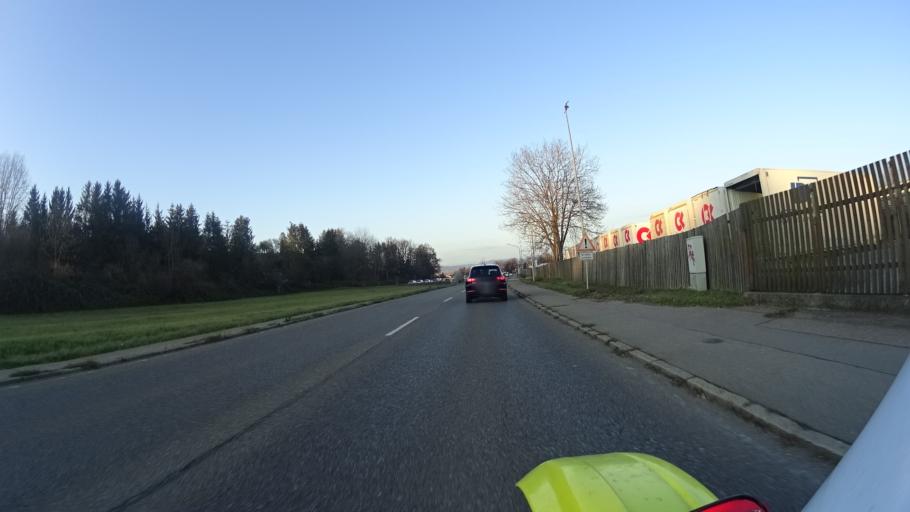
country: DE
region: Baden-Wuerttemberg
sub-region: Regierungsbezirk Stuttgart
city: Eislingen
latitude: 48.6768
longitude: 9.6877
